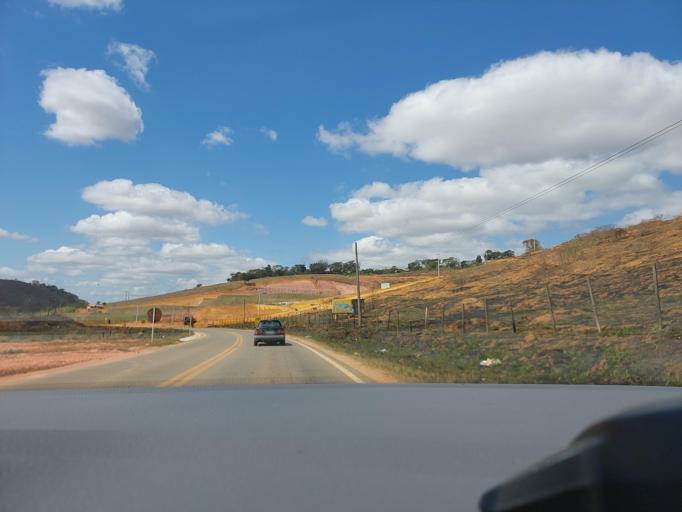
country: BR
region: Minas Gerais
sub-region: Muriae
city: Muriae
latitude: -21.1131
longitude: -42.4421
